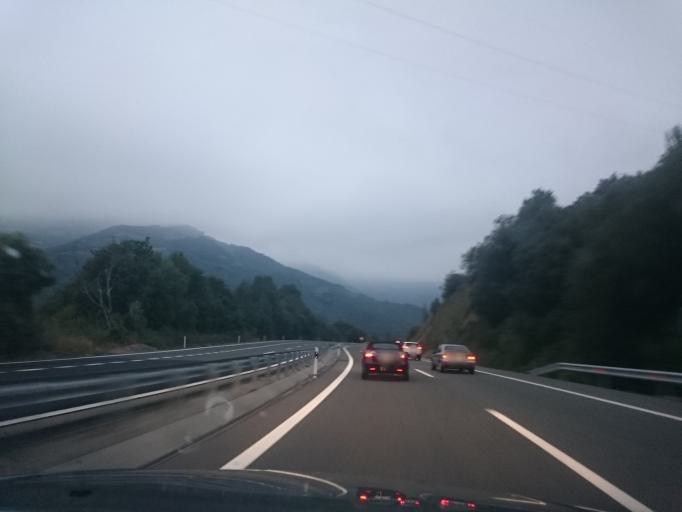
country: ES
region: Asturias
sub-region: Province of Asturias
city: Pola de Lena
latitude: 43.0653
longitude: -5.8221
